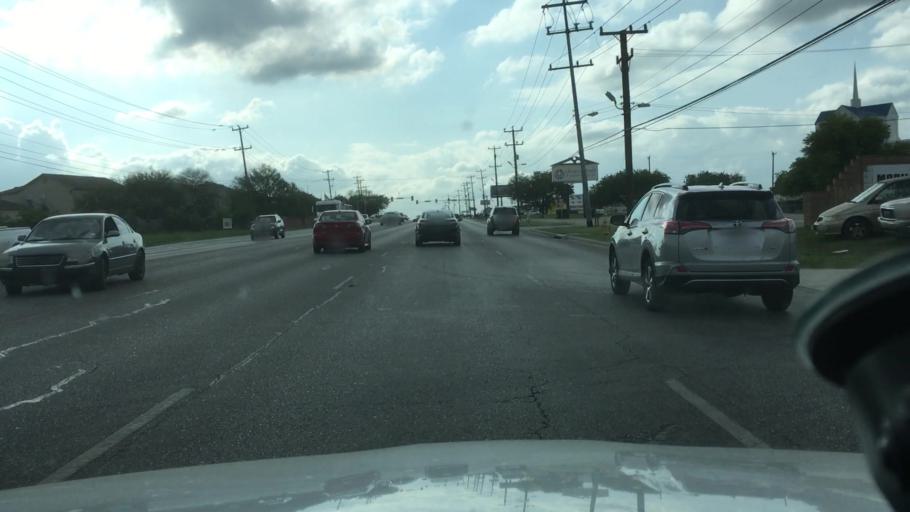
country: US
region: Texas
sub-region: Bexar County
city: Windcrest
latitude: 29.5011
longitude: -98.3569
